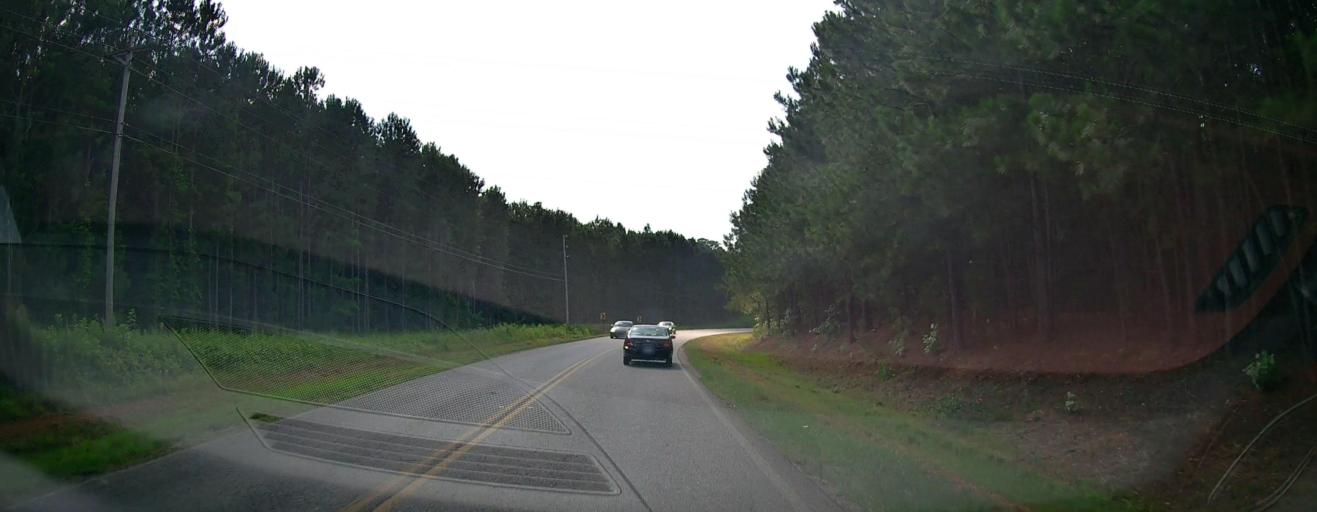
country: US
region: Georgia
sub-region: Henry County
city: McDonough
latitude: 33.4403
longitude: -84.2087
